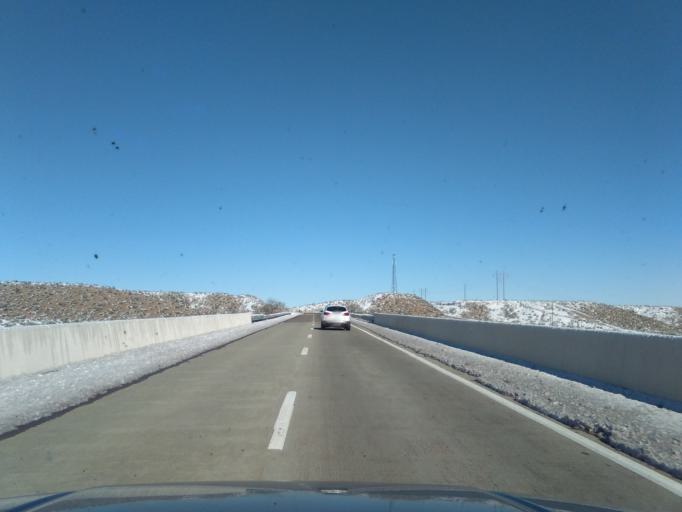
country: US
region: New Mexico
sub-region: Socorro County
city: Socorro
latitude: 33.6607
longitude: -107.0918
